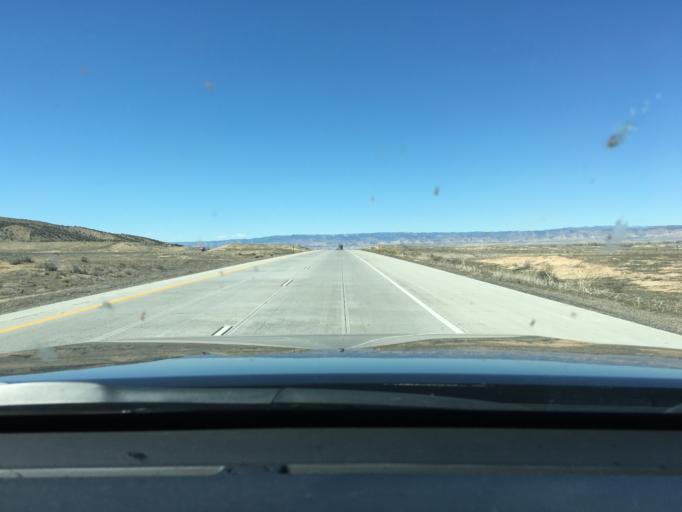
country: US
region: Colorado
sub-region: Mesa County
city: Loma
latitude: 39.2022
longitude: -108.8525
